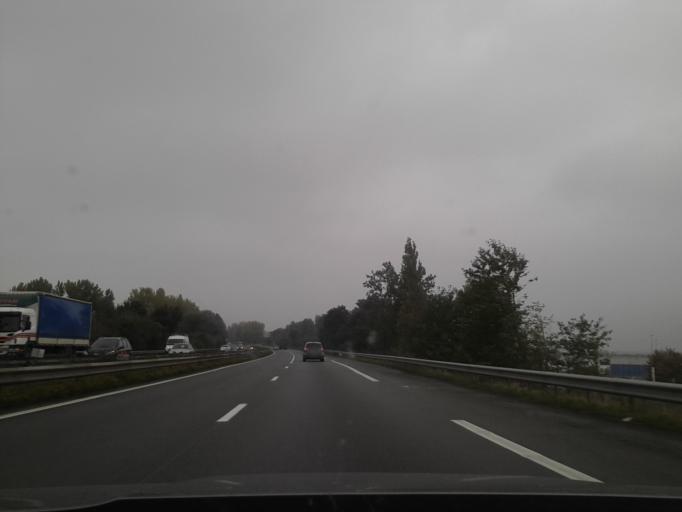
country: FR
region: Nord-Pas-de-Calais
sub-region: Departement du Nord
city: Lieu-Saint-Amand
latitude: 50.2747
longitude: 3.3370
